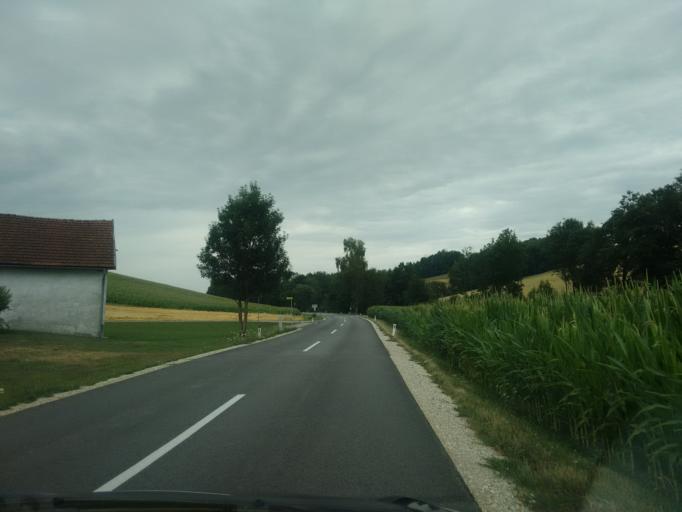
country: AT
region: Upper Austria
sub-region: Politischer Bezirk Grieskirchen
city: Grieskirchen
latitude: 48.2001
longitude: 13.8564
